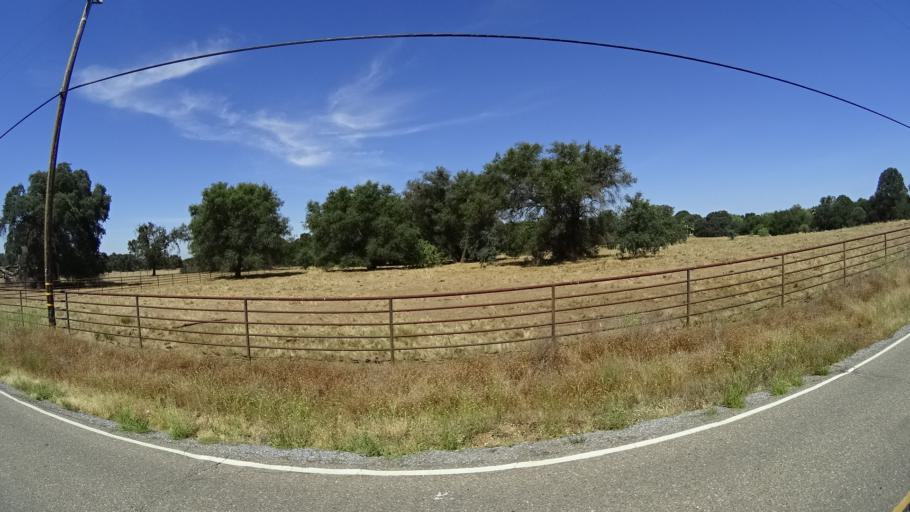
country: US
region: California
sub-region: Calaveras County
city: Rancho Calaveras
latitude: 38.1428
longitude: -120.8992
